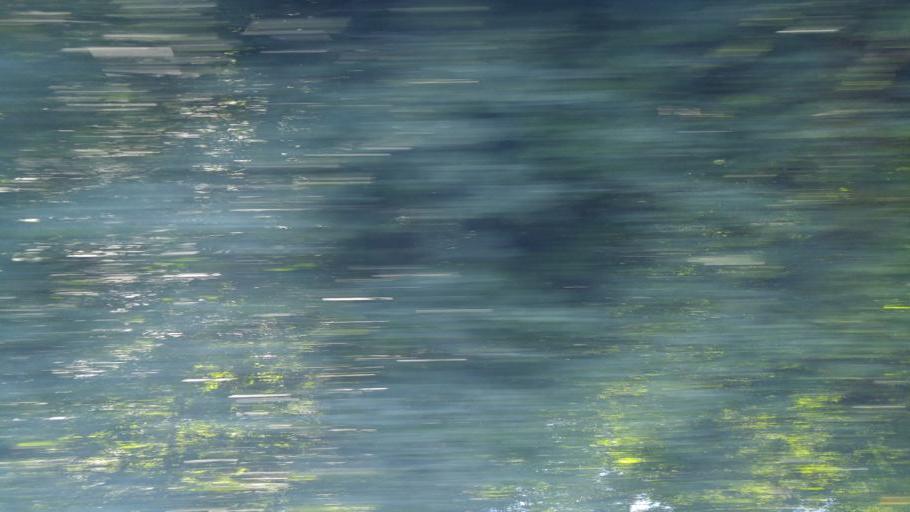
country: NO
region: Sor-Trondelag
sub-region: Midtre Gauldal
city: Storen
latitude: 63.0382
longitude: 10.2974
